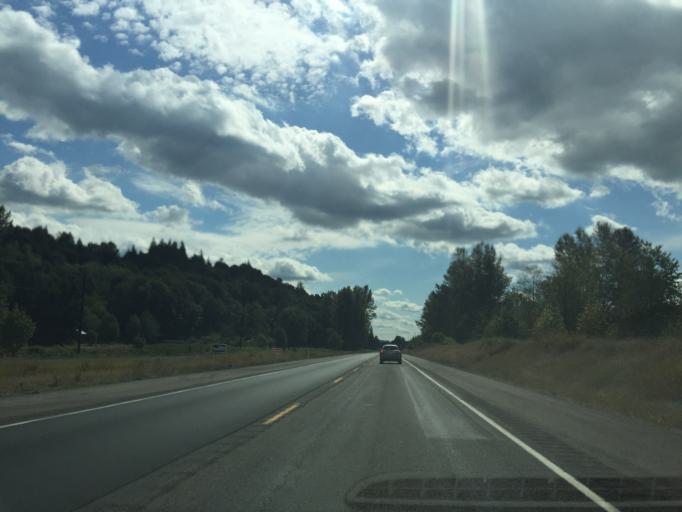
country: US
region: Washington
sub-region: Snohomish County
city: Snohomish
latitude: 47.9308
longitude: -122.0720
